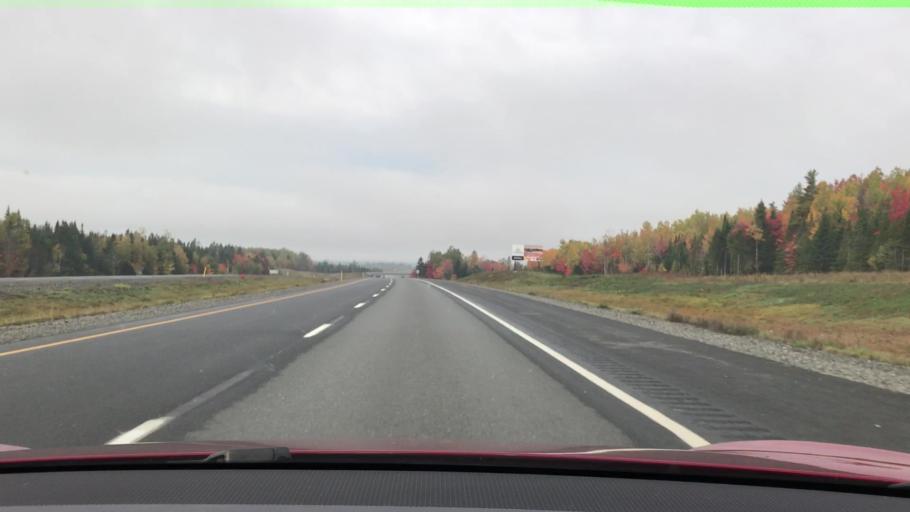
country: US
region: Maine
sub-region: Washington County
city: Calais
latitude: 45.2197
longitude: -67.2274
